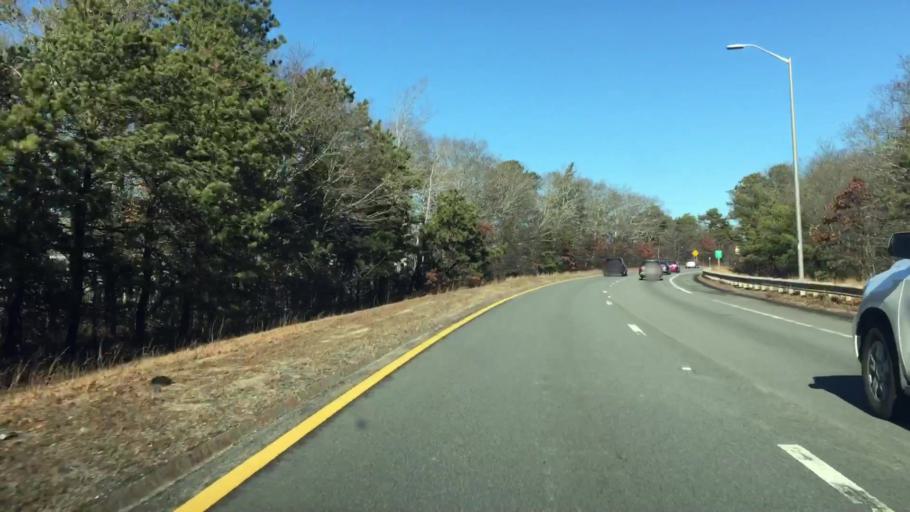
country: US
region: Massachusetts
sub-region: Barnstable County
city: Pocasset
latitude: 41.6872
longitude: -70.5904
